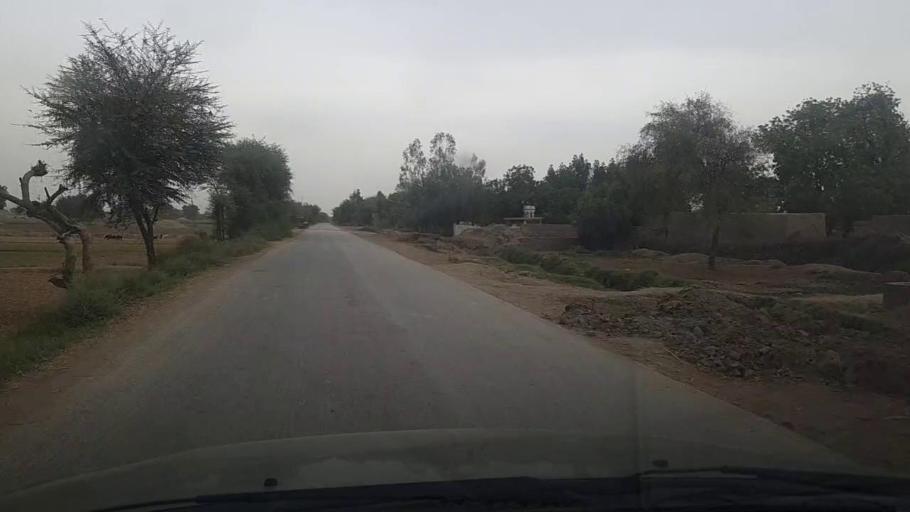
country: PK
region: Sindh
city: Daulatpur
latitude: 26.3226
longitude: 68.1069
